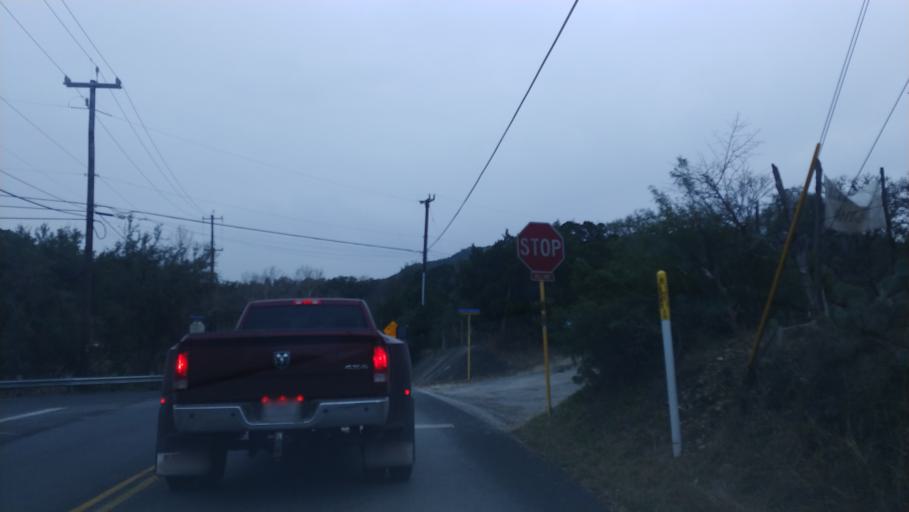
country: US
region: Texas
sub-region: Bexar County
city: Helotes
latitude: 29.6065
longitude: -98.6861
